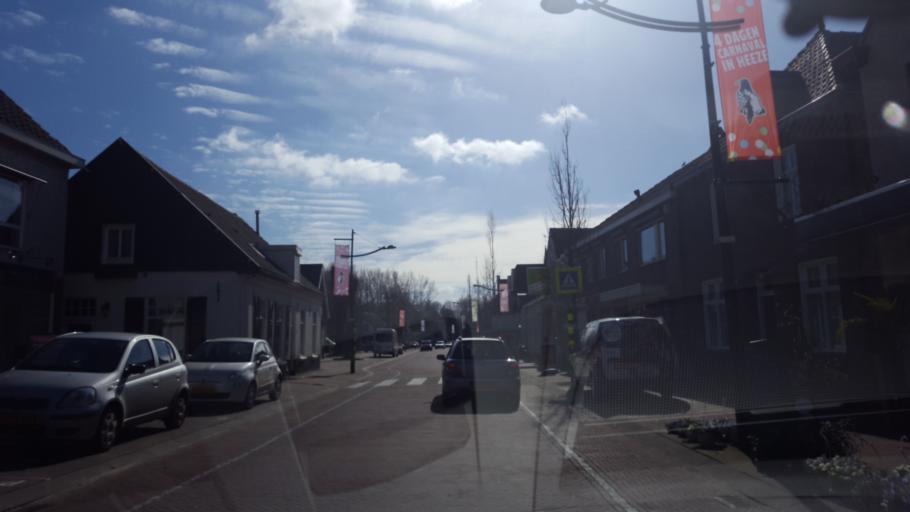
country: NL
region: North Brabant
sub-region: Gemeente Heeze-Leende
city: Heeze
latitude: 51.3844
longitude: 5.5798
